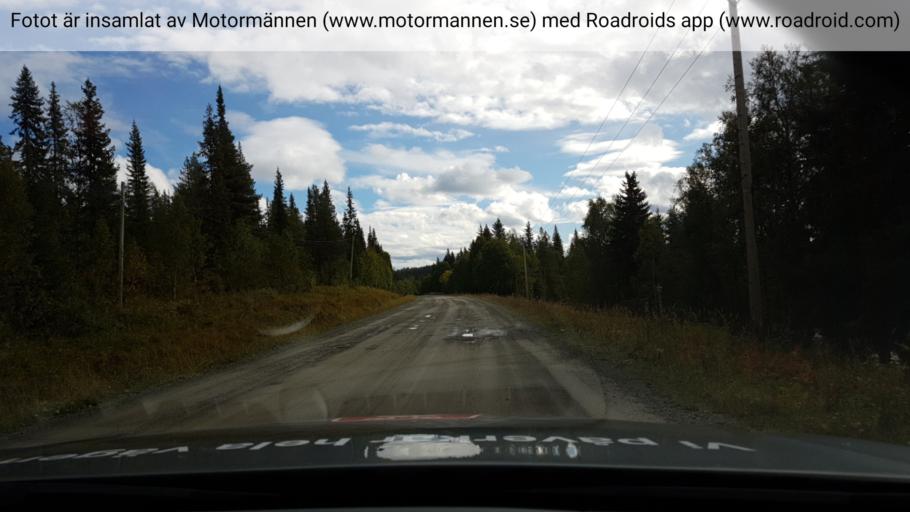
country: SE
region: Jaemtland
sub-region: Are Kommun
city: Are
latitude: 63.6923
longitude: 12.8009
